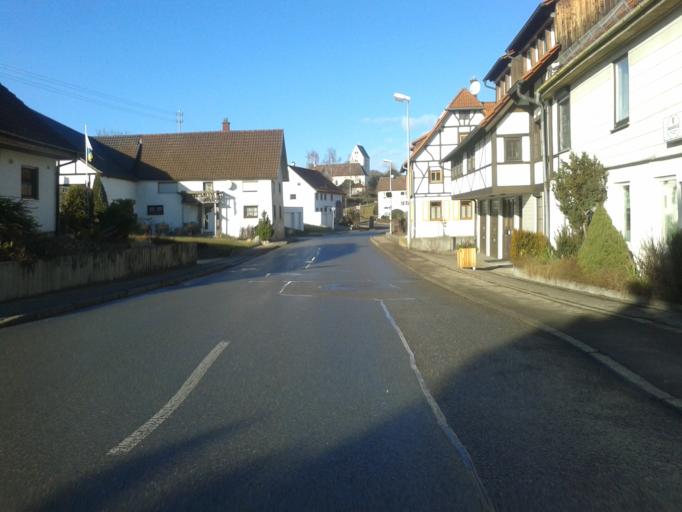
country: DE
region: Baden-Wuerttemberg
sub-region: Tuebingen Region
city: Erbach
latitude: 48.3959
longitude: 9.8620
